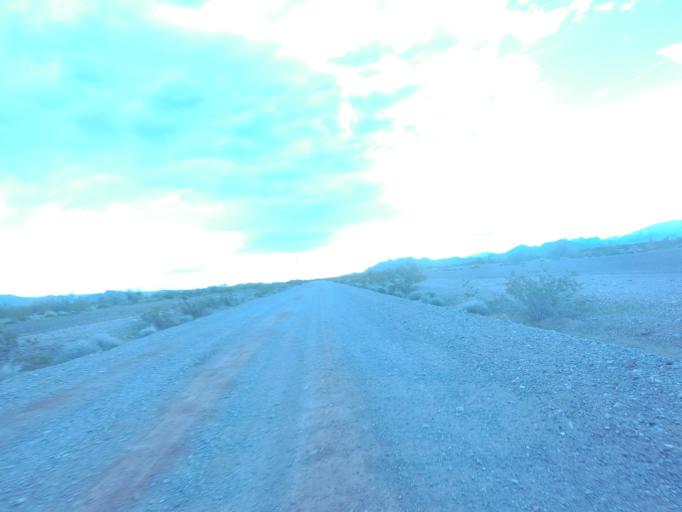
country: US
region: Arizona
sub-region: La Paz County
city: Quartzsite
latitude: 33.5345
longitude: -114.2009
